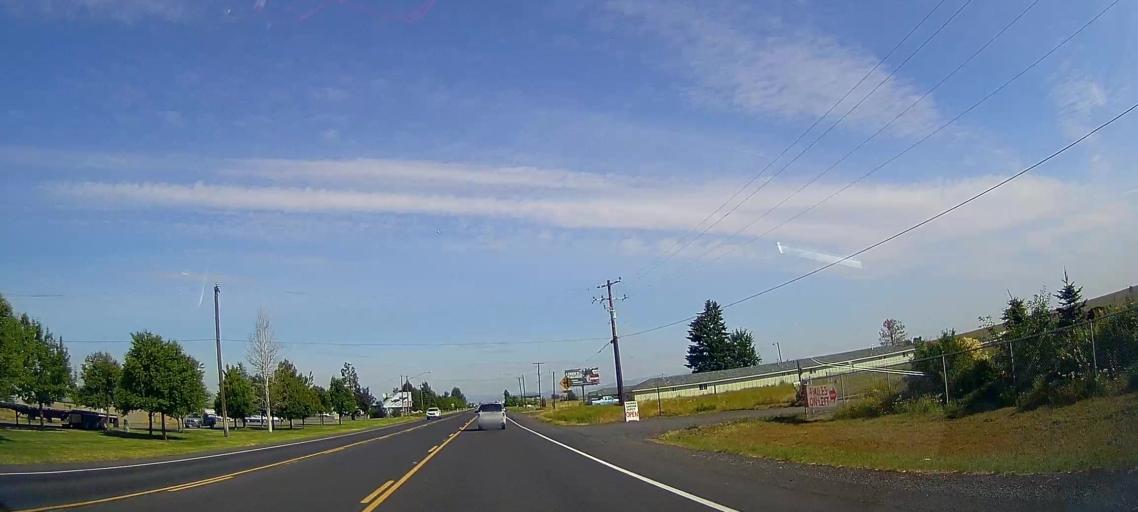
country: US
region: Oregon
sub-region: Jefferson County
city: Madras
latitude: 44.6597
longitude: -121.1324
